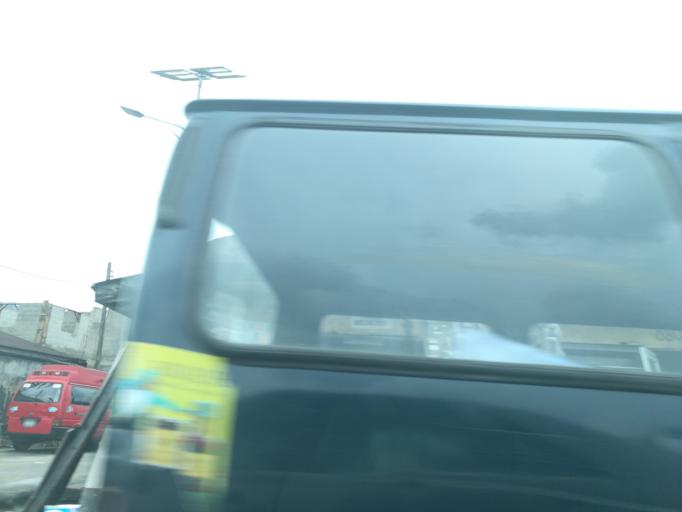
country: NG
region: Rivers
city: Port Harcourt
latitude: 4.8072
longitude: 6.9908
